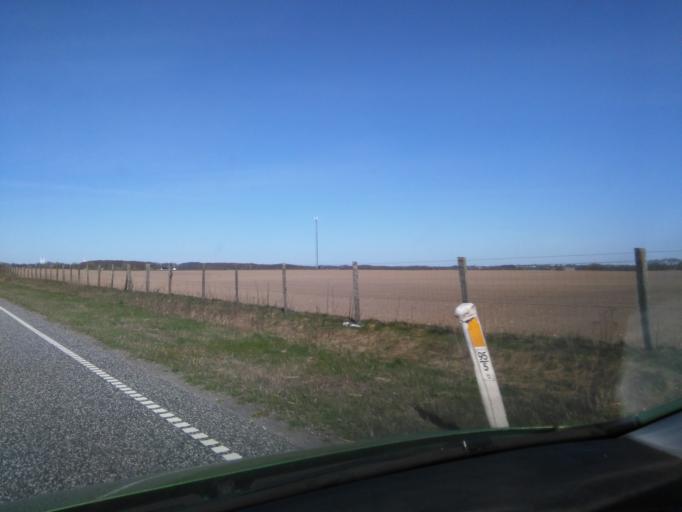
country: DK
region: Central Jutland
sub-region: Hedensted Kommune
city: Hedensted
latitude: 55.8443
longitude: 9.6645
